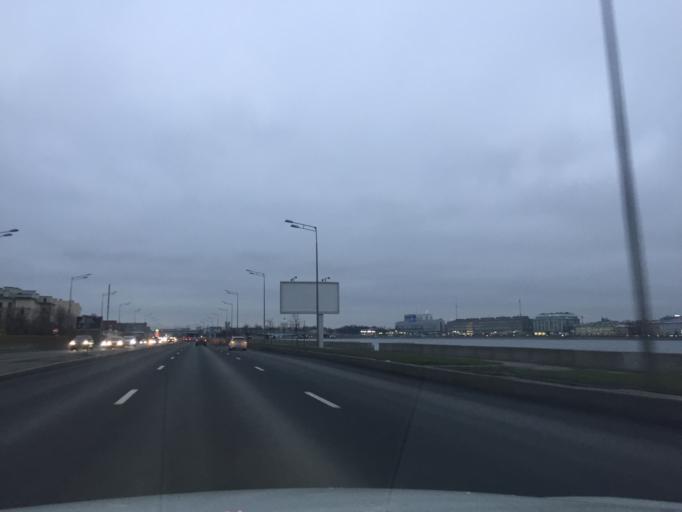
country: RU
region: St.-Petersburg
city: Centralniy
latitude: 59.9347
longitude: 30.4014
